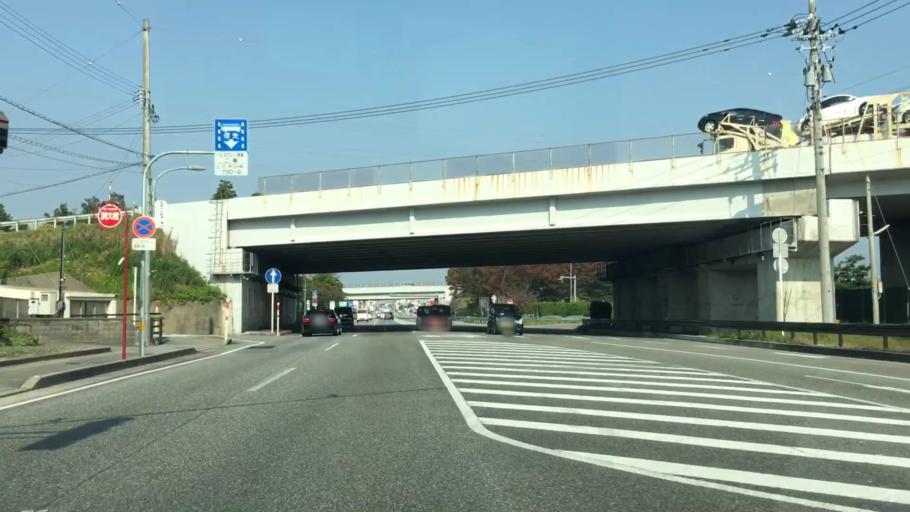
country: JP
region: Toyama
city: Toyama-shi
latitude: 36.6523
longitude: 137.2097
